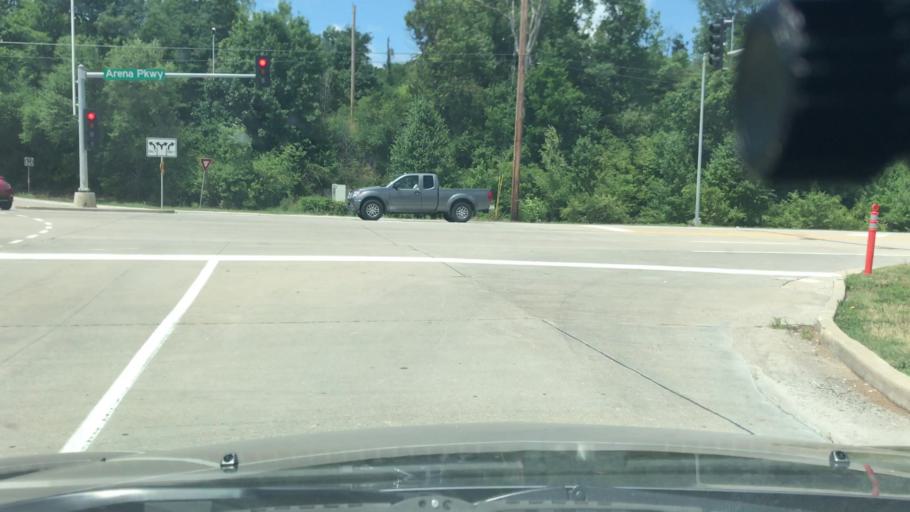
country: US
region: Missouri
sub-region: Saint Charles County
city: Saint Charles
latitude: 38.7476
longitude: -90.5106
